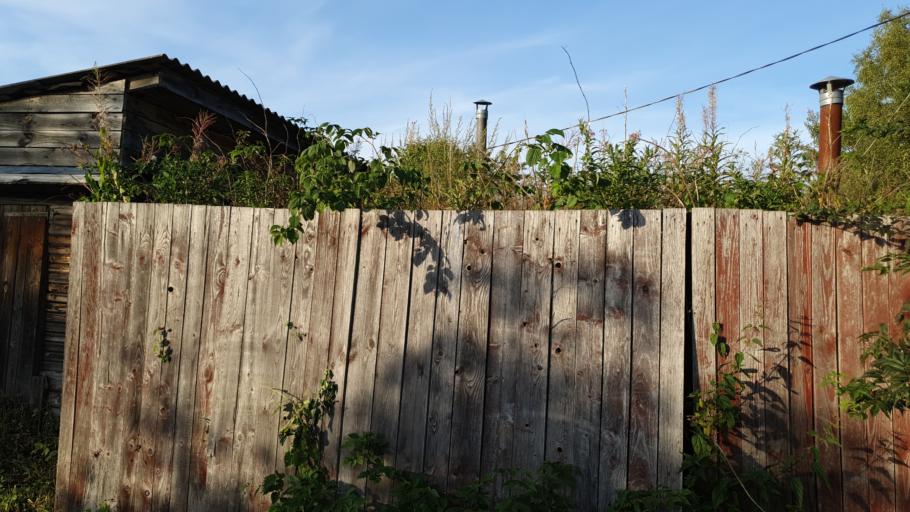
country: RU
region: Leningrad
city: Ivangorod
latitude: 59.4280
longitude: 28.3237
